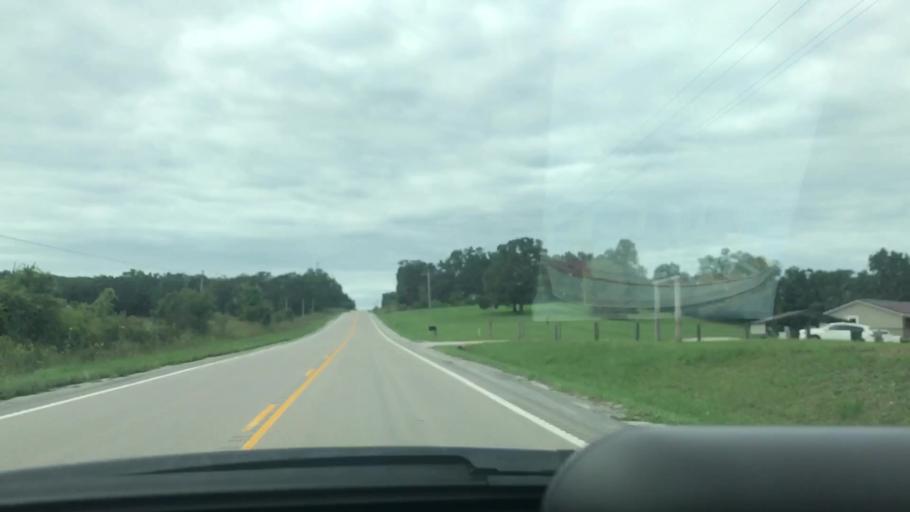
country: US
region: Missouri
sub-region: Benton County
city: Warsaw
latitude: 38.1365
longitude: -93.2833
